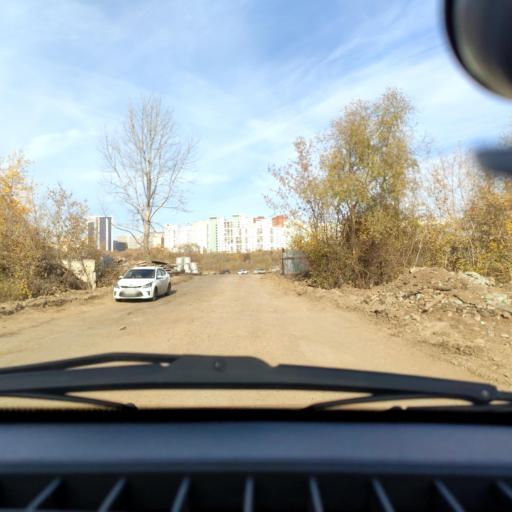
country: RU
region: Bashkortostan
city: Ufa
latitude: 54.6850
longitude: 55.9867
